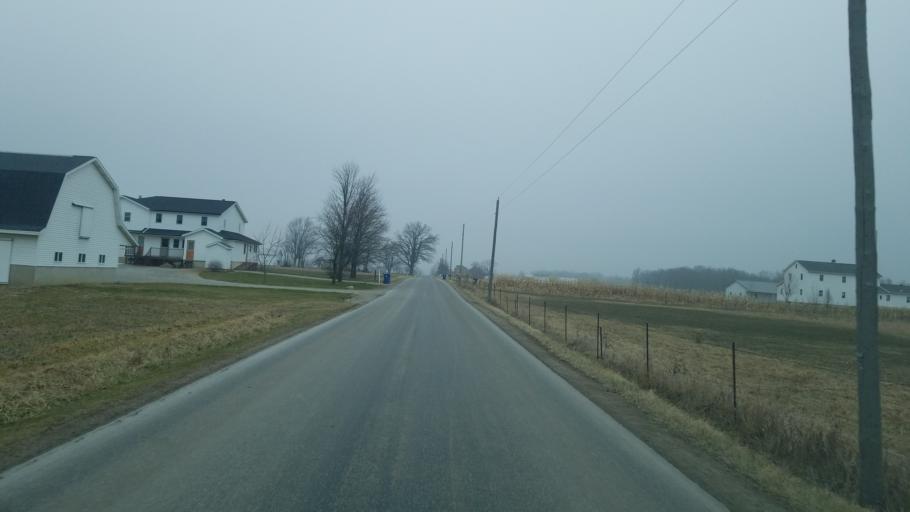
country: US
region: Indiana
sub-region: Adams County
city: Berne
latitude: 40.7213
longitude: -84.9751
